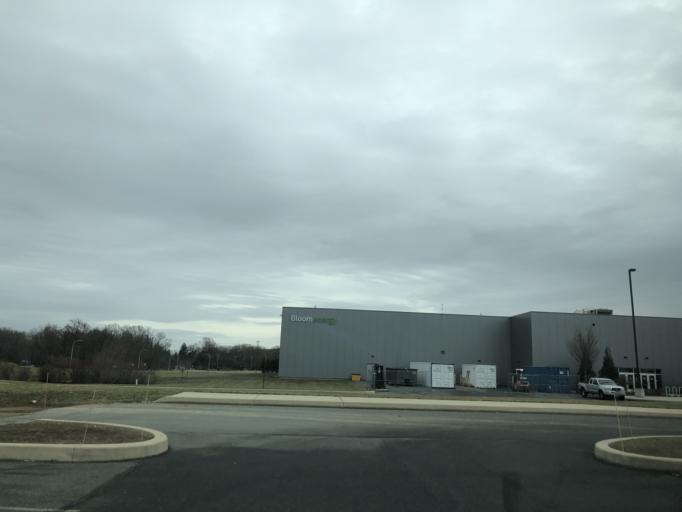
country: US
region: Delaware
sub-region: New Castle County
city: Newark
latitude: 39.6629
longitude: -75.7600
